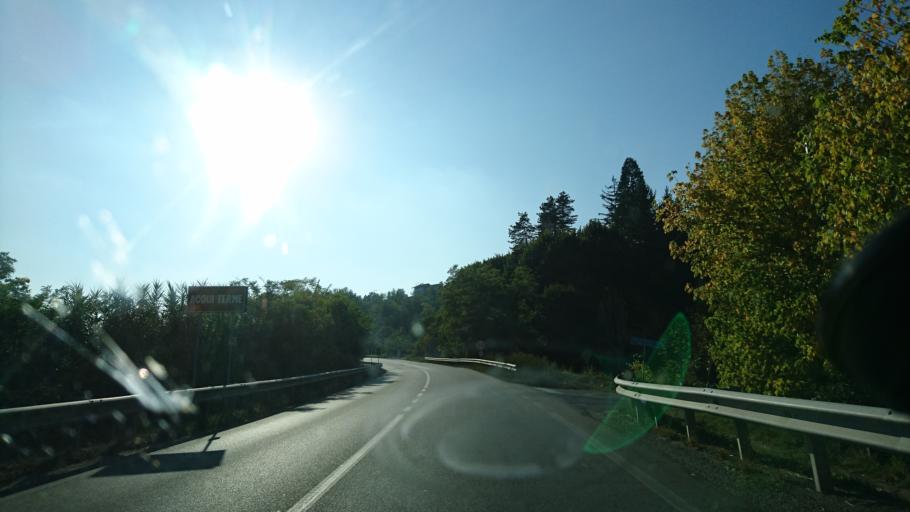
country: IT
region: Piedmont
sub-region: Provincia di Alessandria
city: Terzo
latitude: 44.6758
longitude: 8.4332
